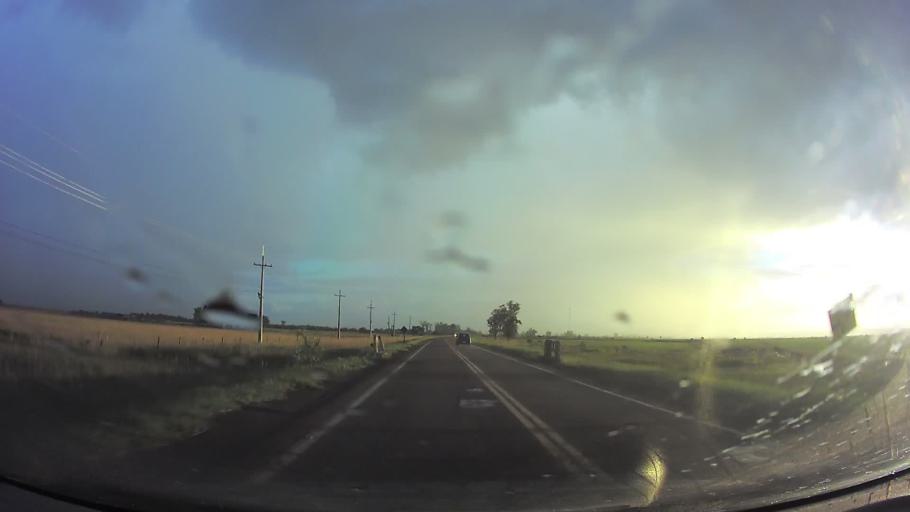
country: PY
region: Paraguari
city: Paraguari
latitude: -25.6820
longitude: -57.1677
